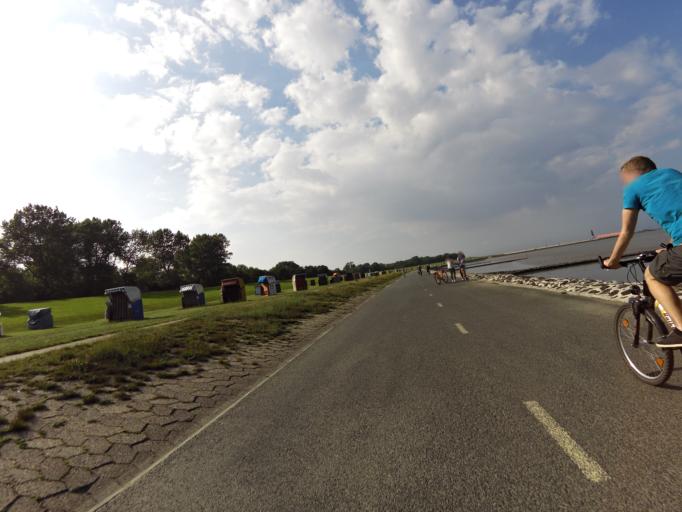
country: DE
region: Lower Saxony
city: Cuxhaven
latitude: 53.8827
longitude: 8.6844
